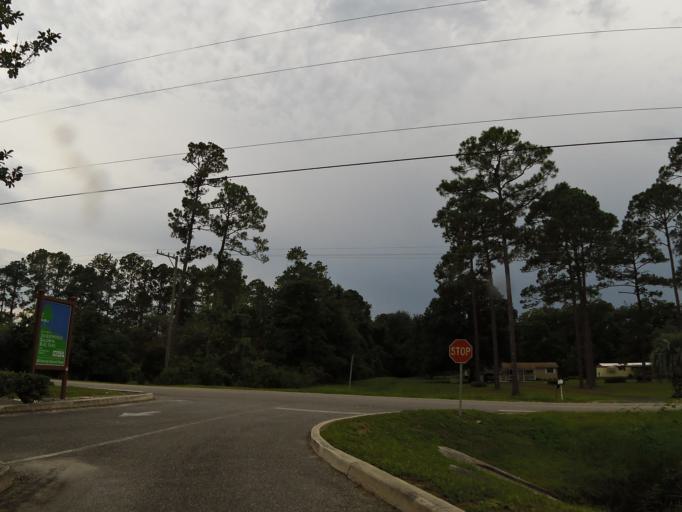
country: US
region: Florida
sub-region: Duval County
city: Baldwin
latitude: 30.3066
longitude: -82.0081
